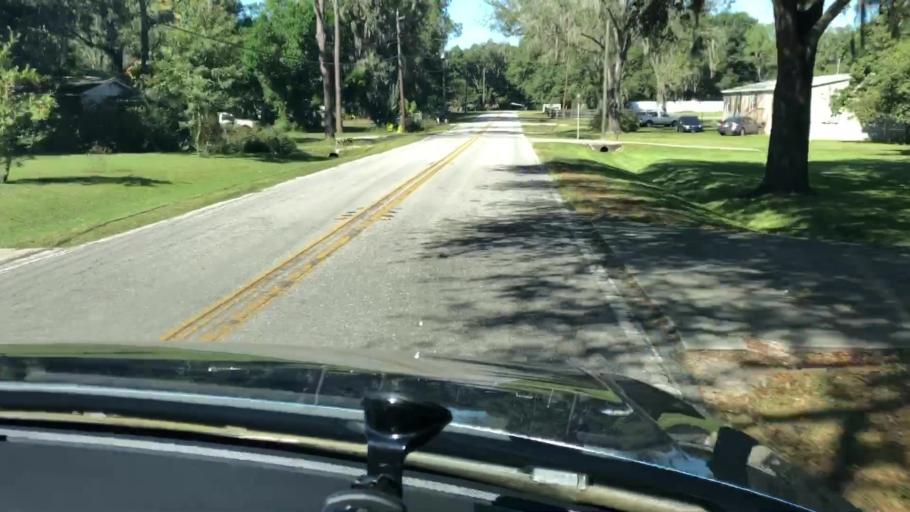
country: US
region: Florida
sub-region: Polk County
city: Kathleen
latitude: 28.1144
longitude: -82.0253
